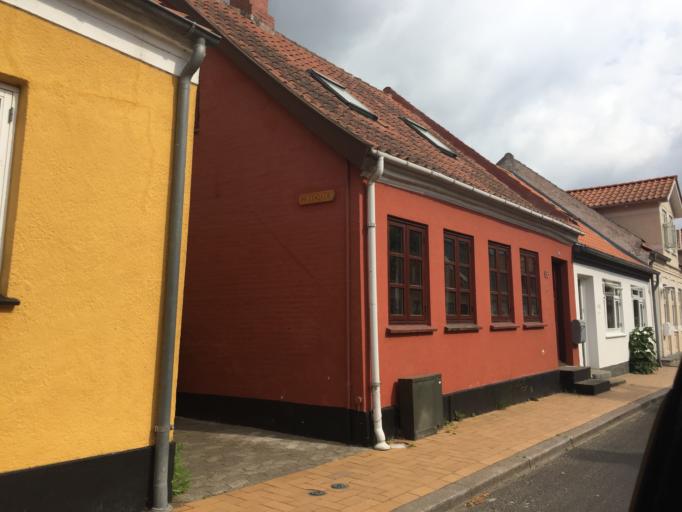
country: DK
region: South Denmark
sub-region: Assens Kommune
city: Assens
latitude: 55.2738
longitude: 9.8922
